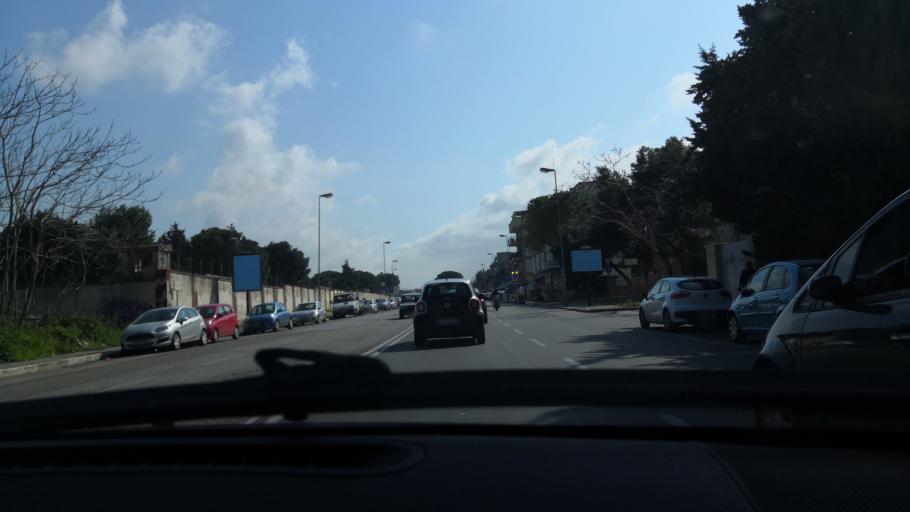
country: IT
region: Apulia
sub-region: Provincia di Bari
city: Bari
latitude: 41.0989
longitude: 16.8737
